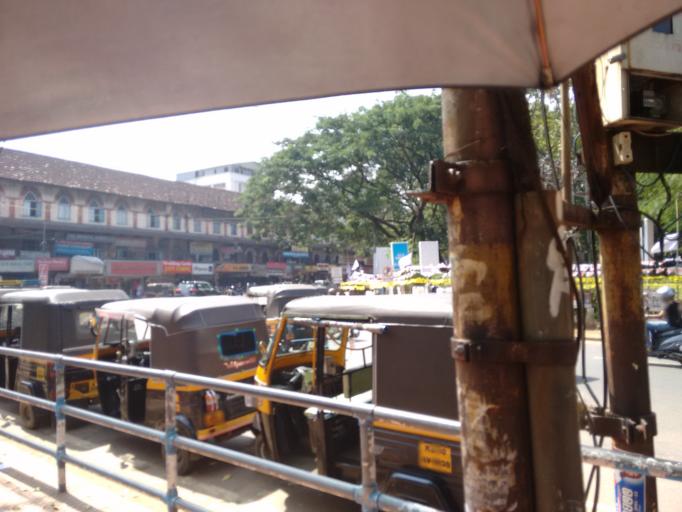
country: IN
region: Kerala
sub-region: Thrissur District
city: Trichur
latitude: 10.5230
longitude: 76.2169
